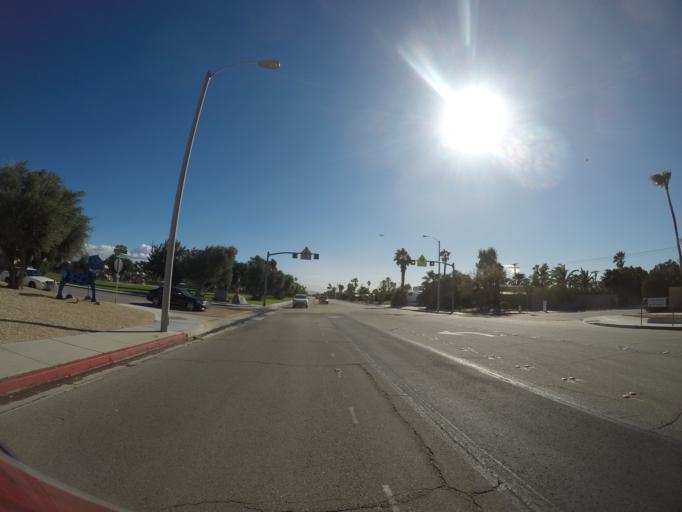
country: US
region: California
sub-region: Riverside County
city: Palm Springs
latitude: 33.8522
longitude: -116.5410
